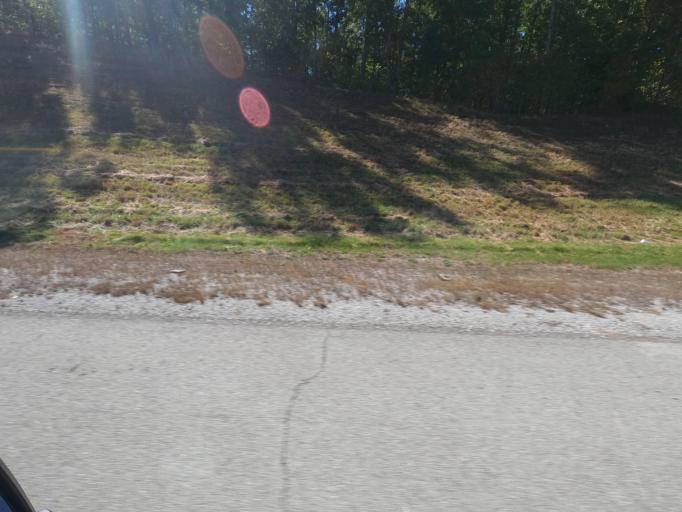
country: US
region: Tennessee
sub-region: Williamson County
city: Fairview
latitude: 35.8882
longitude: -87.1144
